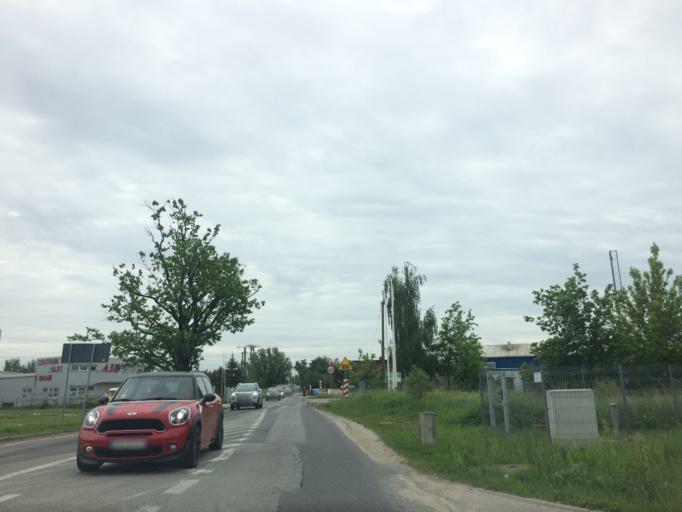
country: PL
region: Lower Silesian Voivodeship
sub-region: Powiat wroclawski
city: Dlugoleka
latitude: 51.1742
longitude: 17.1800
